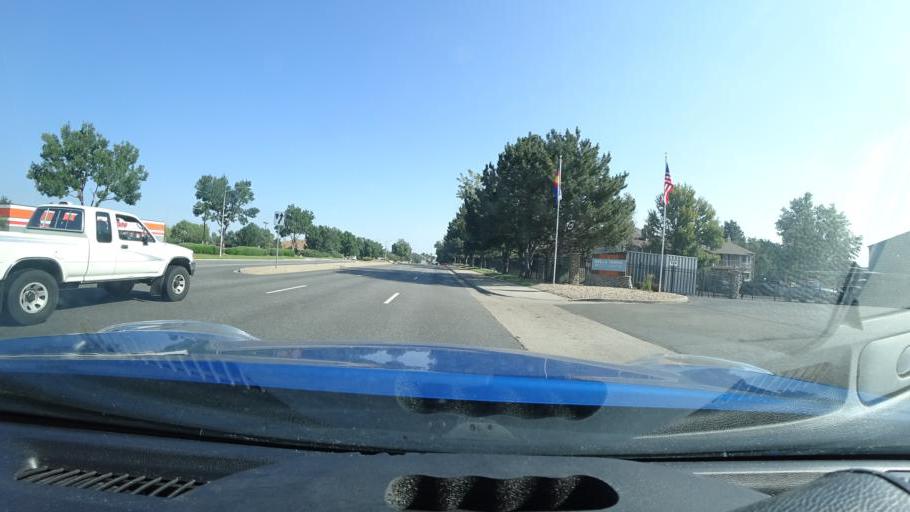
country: US
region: Colorado
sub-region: Adams County
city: Aurora
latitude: 39.6764
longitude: -104.8098
